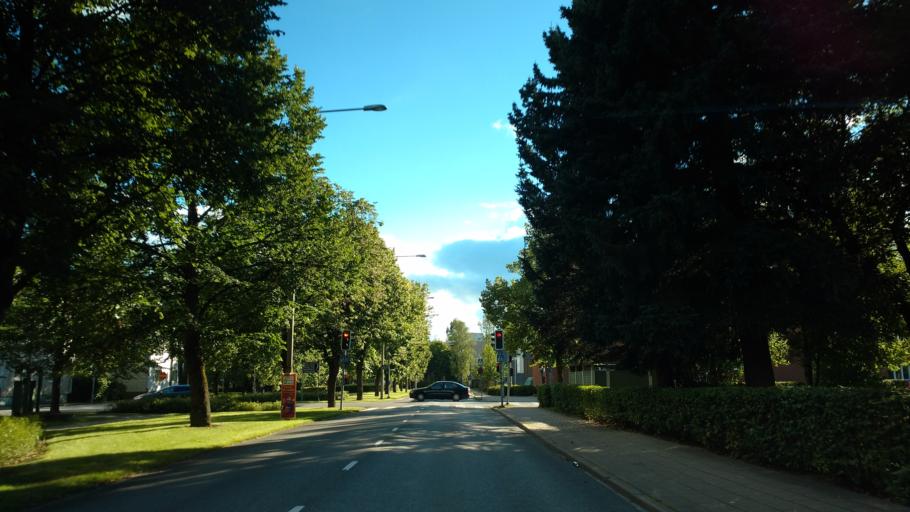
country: FI
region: Varsinais-Suomi
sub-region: Salo
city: Salo
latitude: 60.3886
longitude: 23.1403
